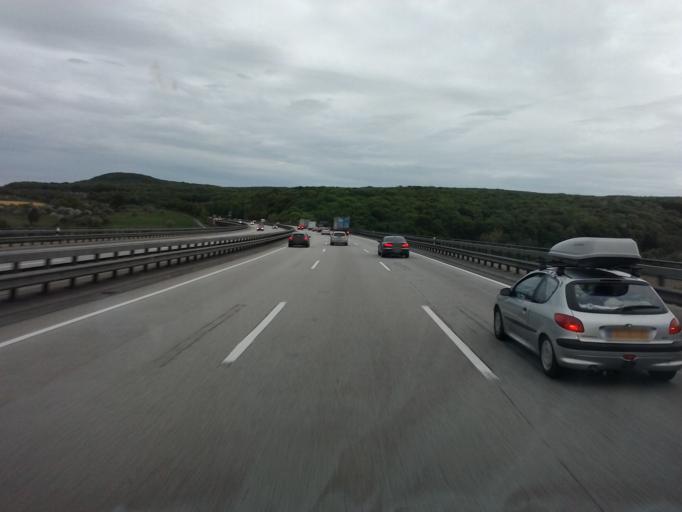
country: DE
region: Rheinland-Pfalz
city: Waldorf
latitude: 50.4882
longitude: 7.2186
